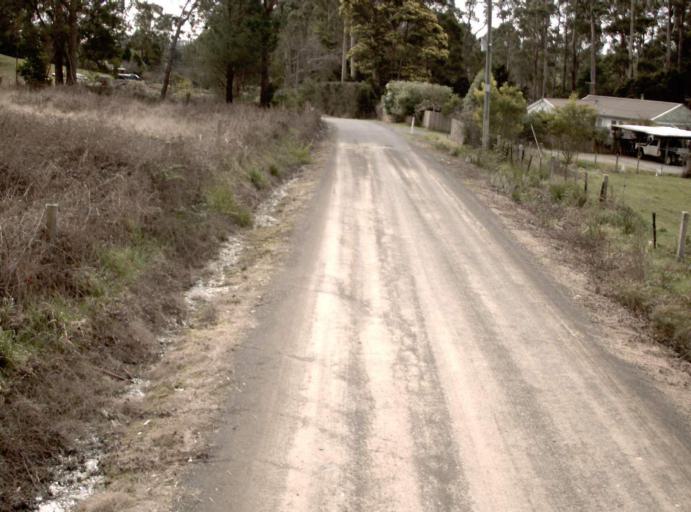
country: AU
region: Tasmania
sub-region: Launceston
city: Mayfield
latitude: -41.2707
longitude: 147.1615
